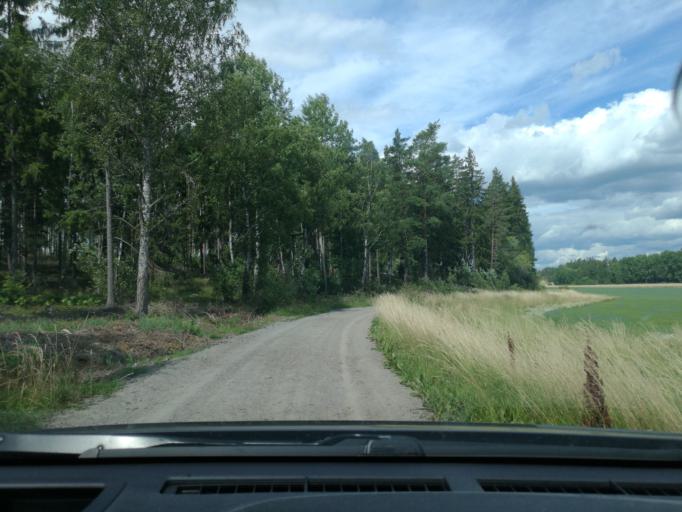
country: SE
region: Stockholm
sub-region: Sigtuna Kommun
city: Marsta
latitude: 59.6096
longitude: 17.8021
